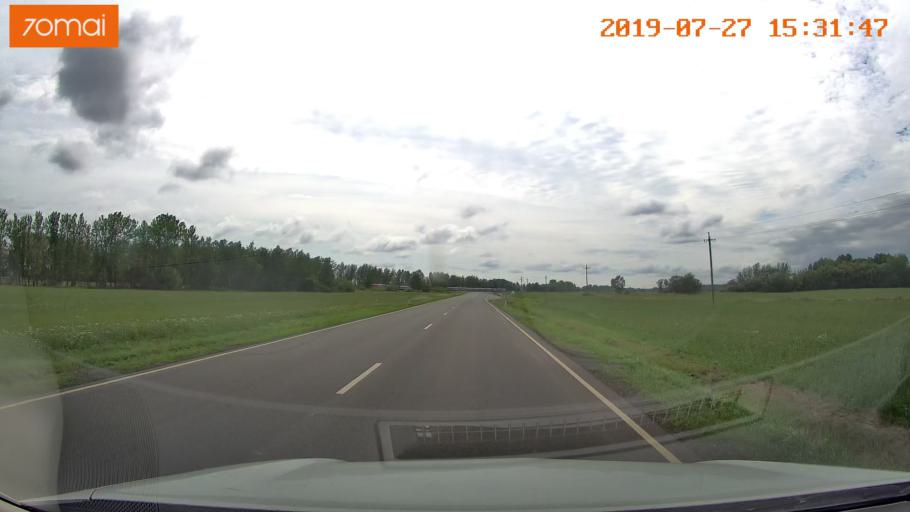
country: RU
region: Kaliningrad
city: Nesterov
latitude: 54.6202
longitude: 22.4852
